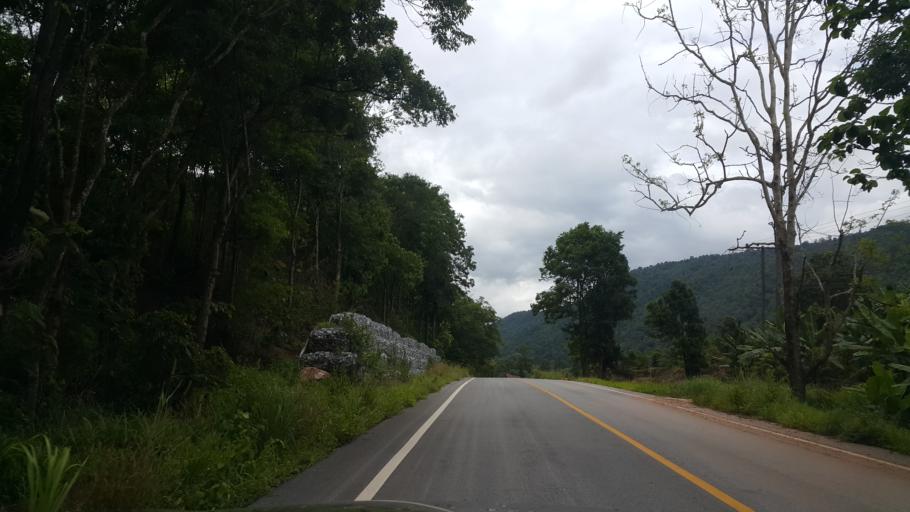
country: TH
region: Phitsanulok
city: Chat Trakan
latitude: 17.3541
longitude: 100.7283
